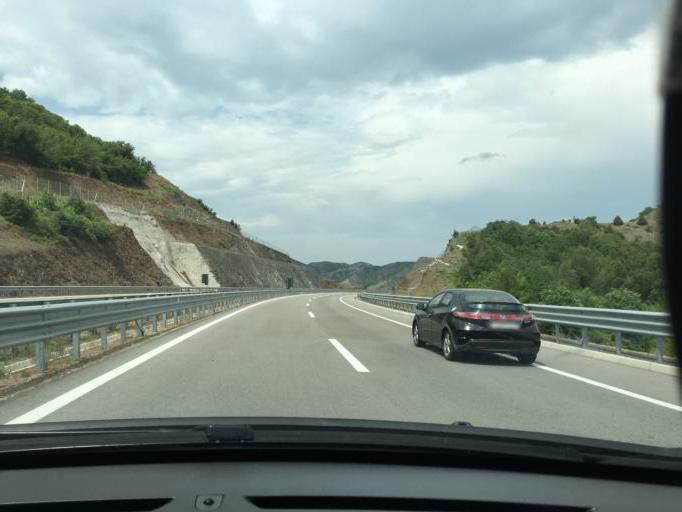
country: MK
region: Gevgelija
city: Miravci
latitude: 41.3600
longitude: 22.3491
